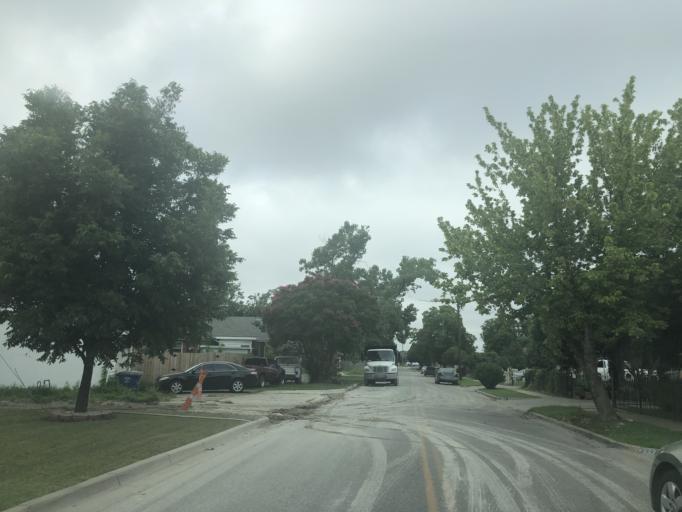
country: US
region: Texas
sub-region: Dallas County
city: University Park
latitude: 32.8679
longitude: -96.8612
